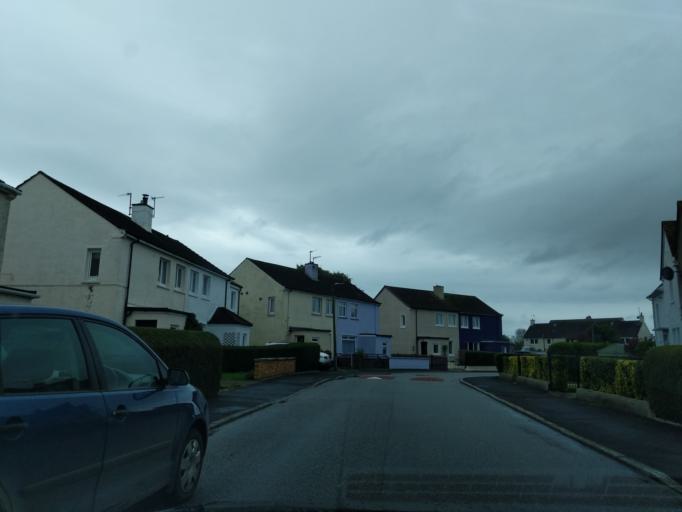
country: GB
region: Scotland
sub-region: Dumfries and Galloway
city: Kirkcudbright
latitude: 54.8339
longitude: -4.0539
